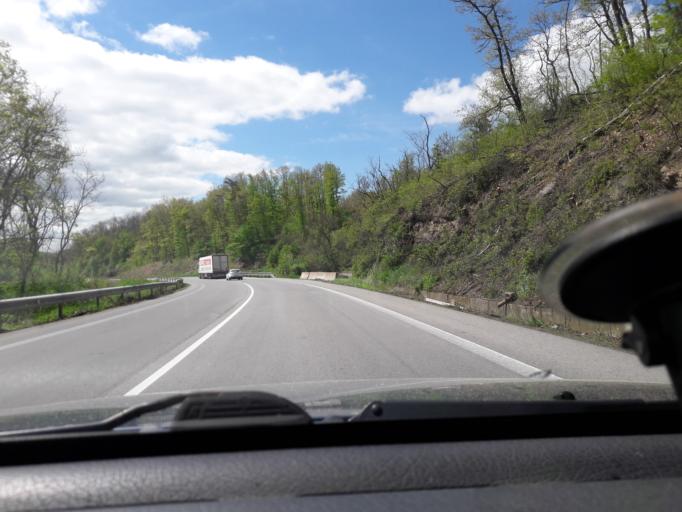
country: SK
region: Banskobystricky
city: Krupina
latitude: 48.3839
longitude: 19.0787
